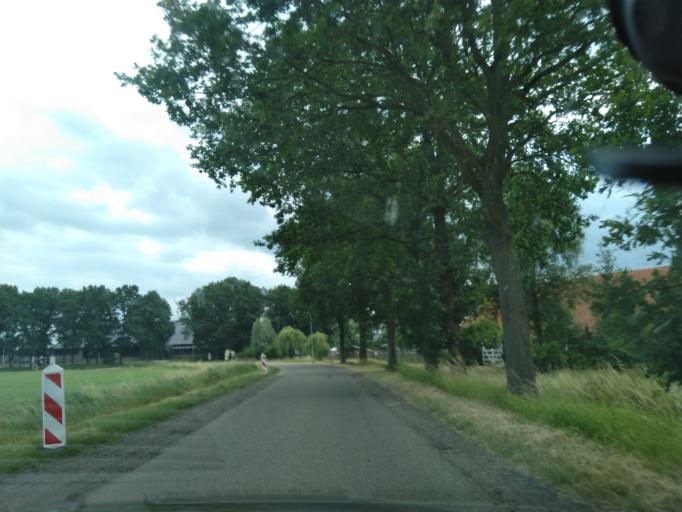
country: NL
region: Groningen
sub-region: Gemeente Vlagtwedde
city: Vlagtwedde
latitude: 53.0948
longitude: 7.0870
